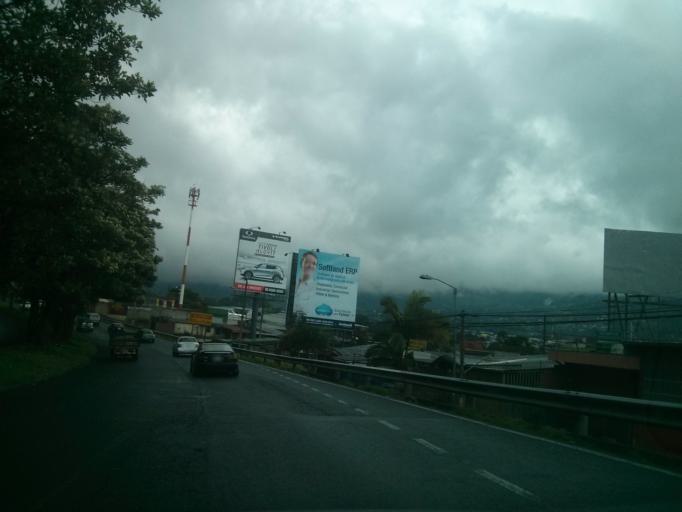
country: CR
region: San Jose
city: San Felipe
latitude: 9.9143
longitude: -84.1058
